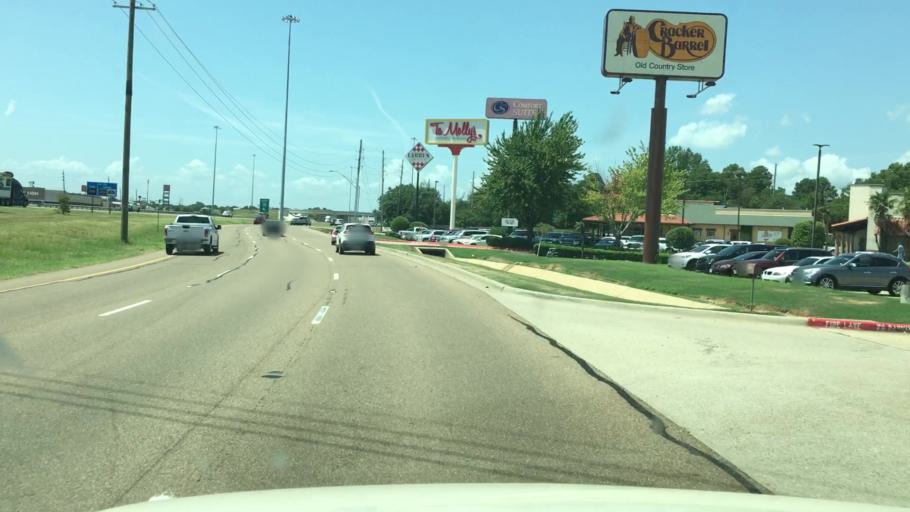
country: US
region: Texas
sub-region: Bowie County
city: Wake Village
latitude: 33.4599
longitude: -94.0808
